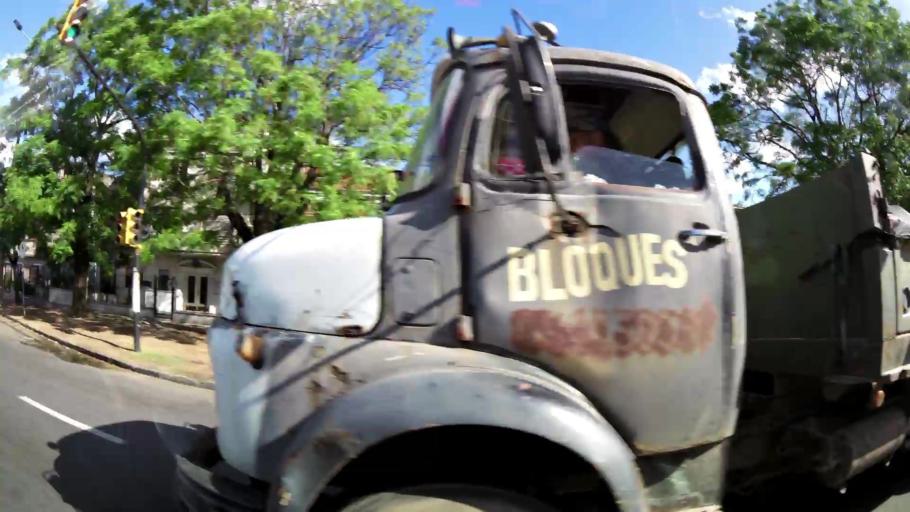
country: UY
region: Montevideo
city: Montevideo
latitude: -34.8726
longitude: -56.2034
